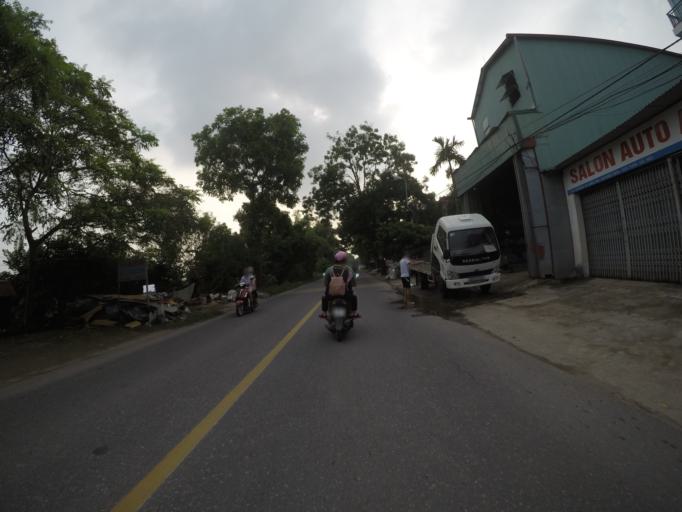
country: VN
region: Ha Noi
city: Soc Son
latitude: 21.2292
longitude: 105.7882
